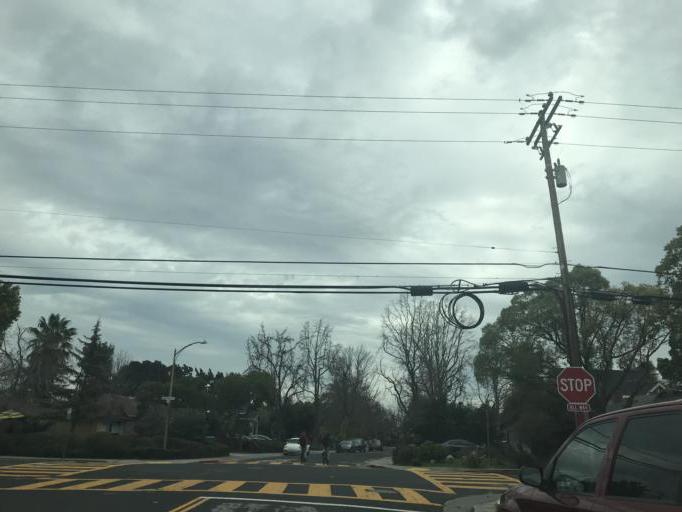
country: US
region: California
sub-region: Santa Clara County
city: Palo Alto
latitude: 37.4249
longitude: -122.1289
